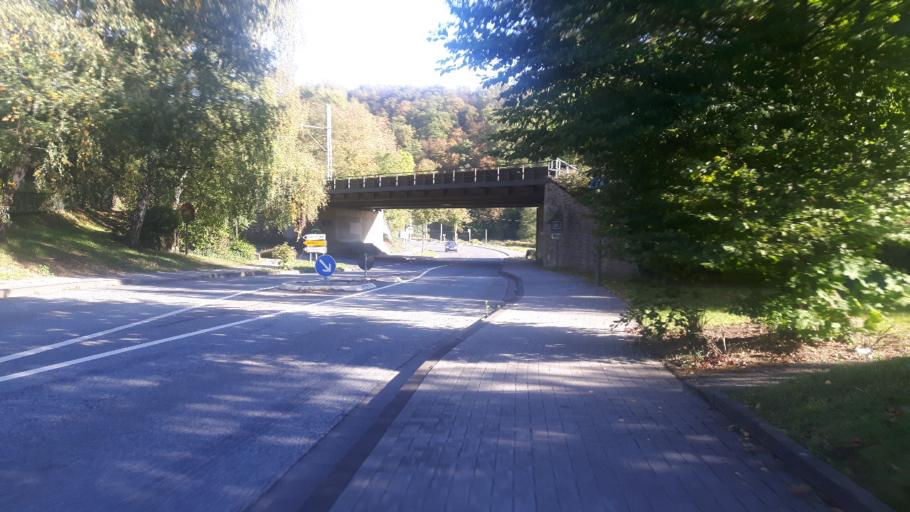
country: DE
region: Rheinland-Pfalz
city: Mittelhof
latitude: 50.7861
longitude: 7.7864
